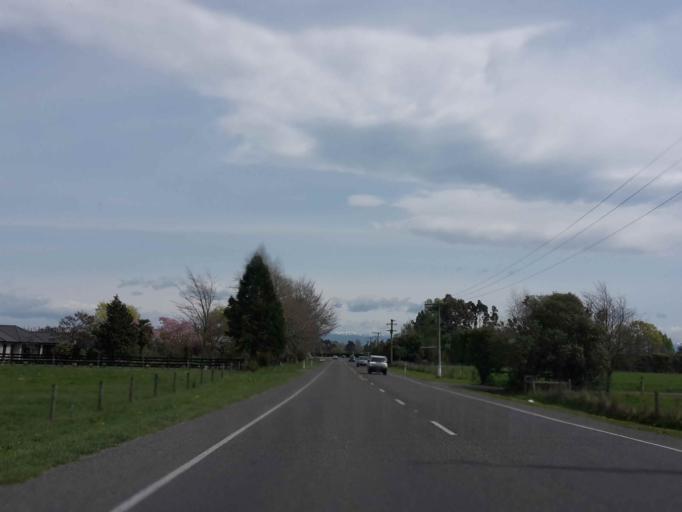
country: NZ
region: Canterbury
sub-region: Waimakariri District
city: Kaiapoi
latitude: -43.3997
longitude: 172.6092
